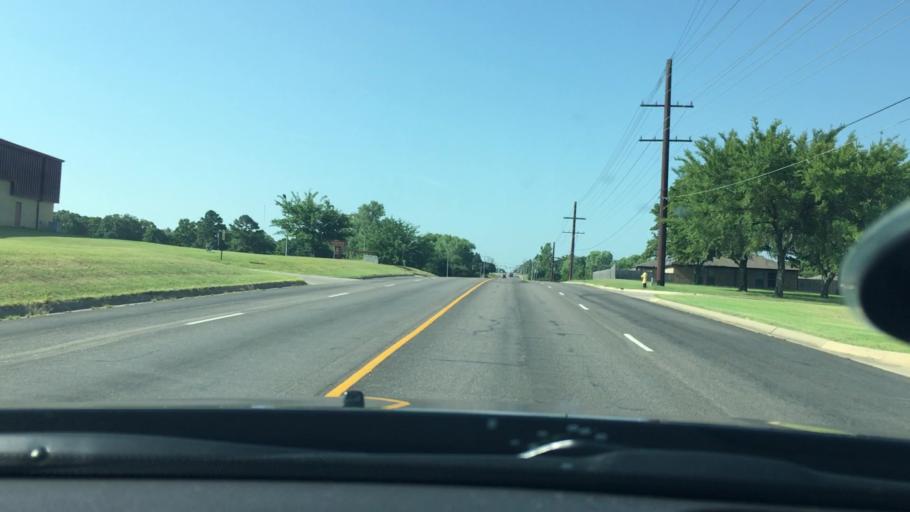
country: US
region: Oklahoma
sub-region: Pontotoc County
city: Ada
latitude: 34.7887
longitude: -96.6348
